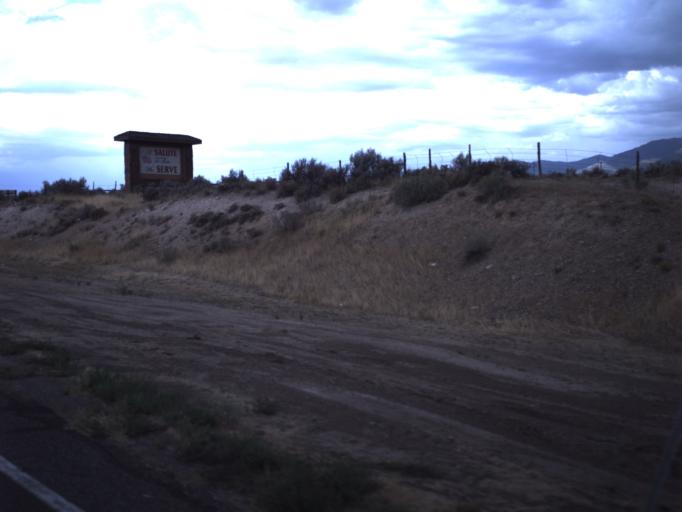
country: US
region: Utah
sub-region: Millard County
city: Fillmore
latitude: 38.9861
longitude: -112.3237
